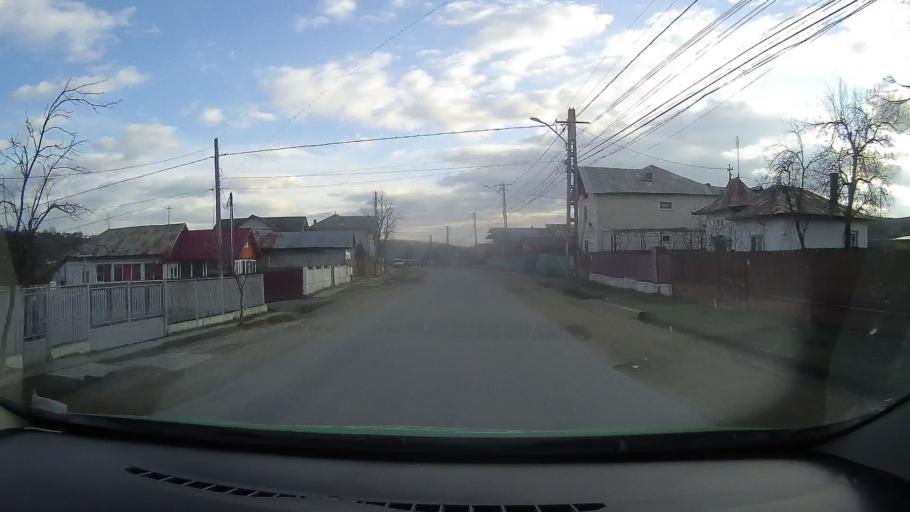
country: RO
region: Dambovita
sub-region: Comuna Ocnita
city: Ocnita
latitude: 44.9871
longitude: 25.5541
